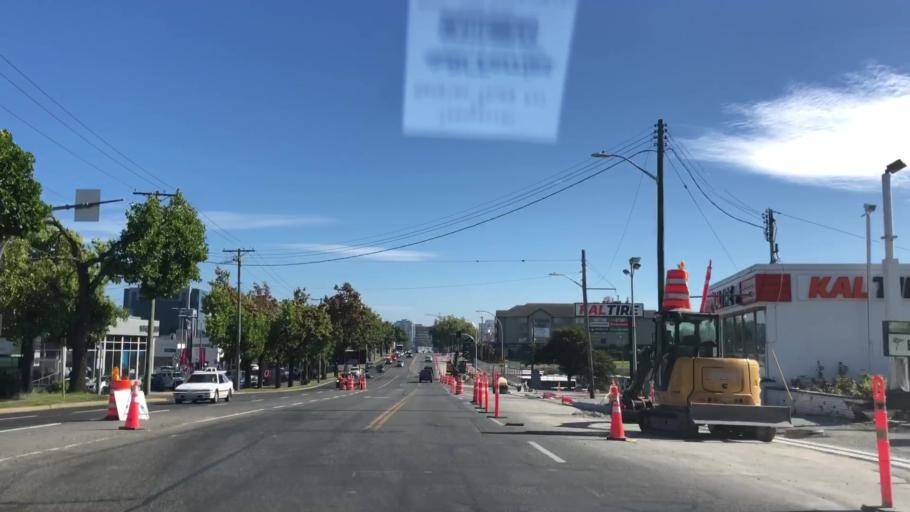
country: CA
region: British Columbia
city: Victoria
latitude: 48.4418
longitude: -123.3689
